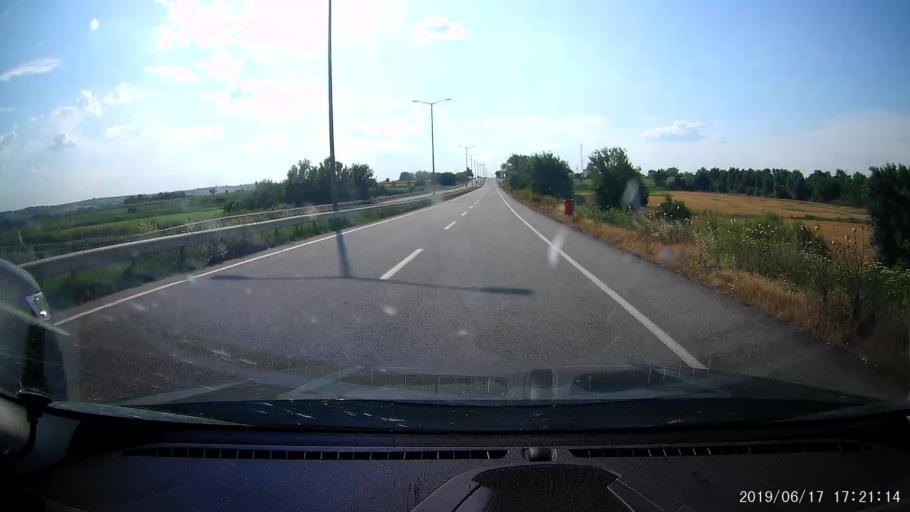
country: GR
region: East Macedonia and Thrace
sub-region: Nomos Evrou
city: Rizia
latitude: 41.7051
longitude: 26.3981
